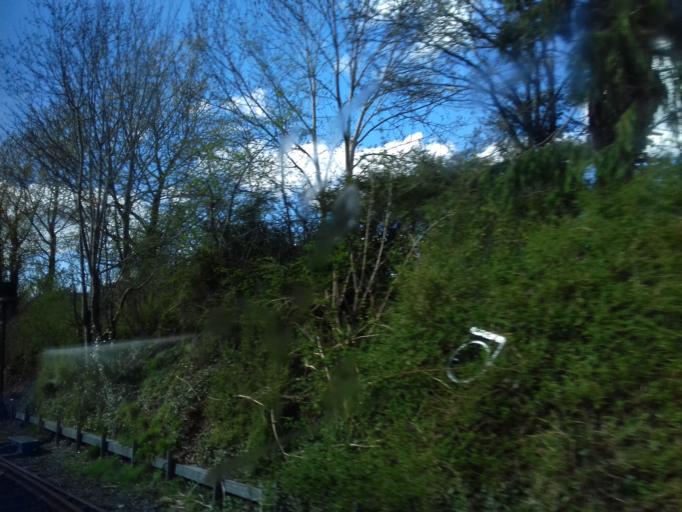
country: IE
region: Munster
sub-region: County Cork
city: Kanturk
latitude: 52.1287
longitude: -8.8949
